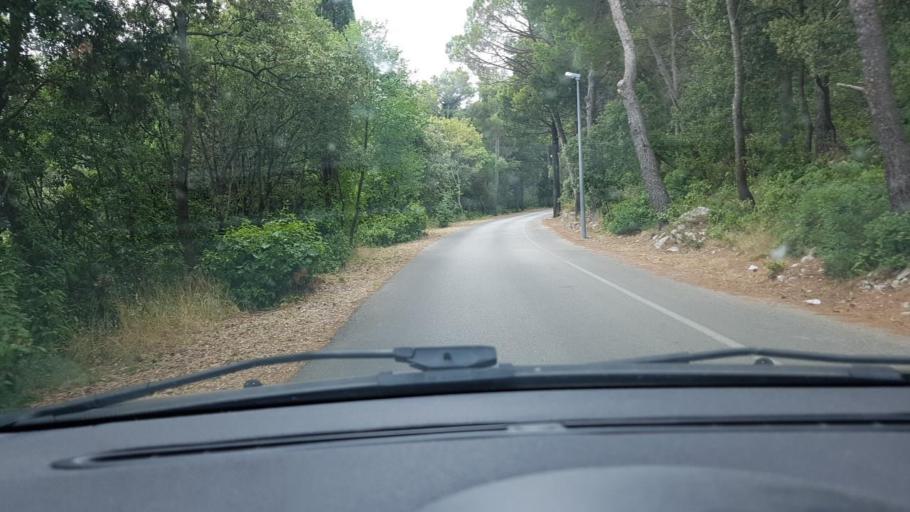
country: HR
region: Dubrovacko-Neretvanska
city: Korcula
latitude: 42.9573
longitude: 17.1314
